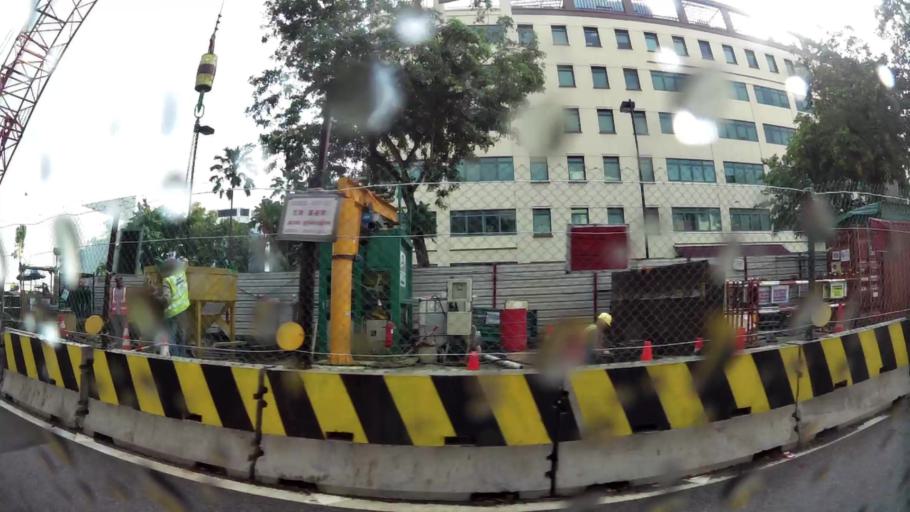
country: SG
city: Singapore
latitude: 1.3312
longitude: 103.9677
